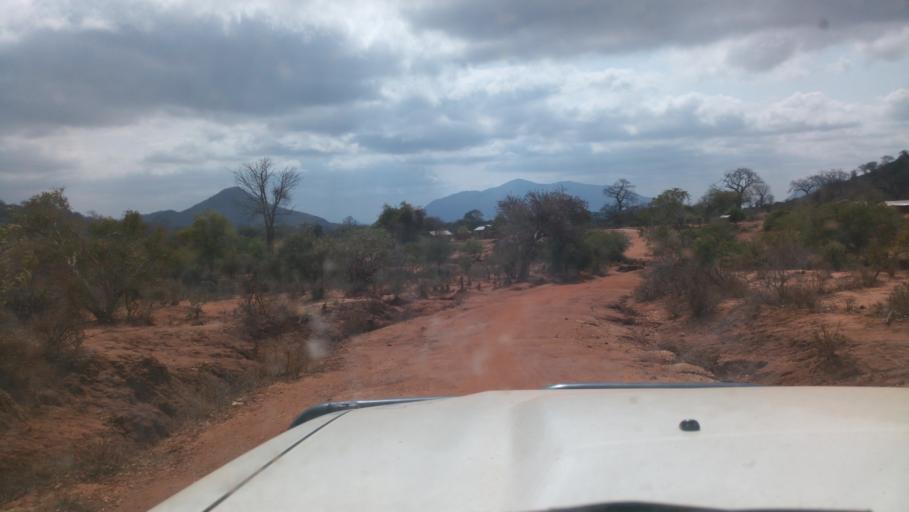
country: KE
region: Kitui
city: Kitui
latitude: -1.8396
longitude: 38.3000
